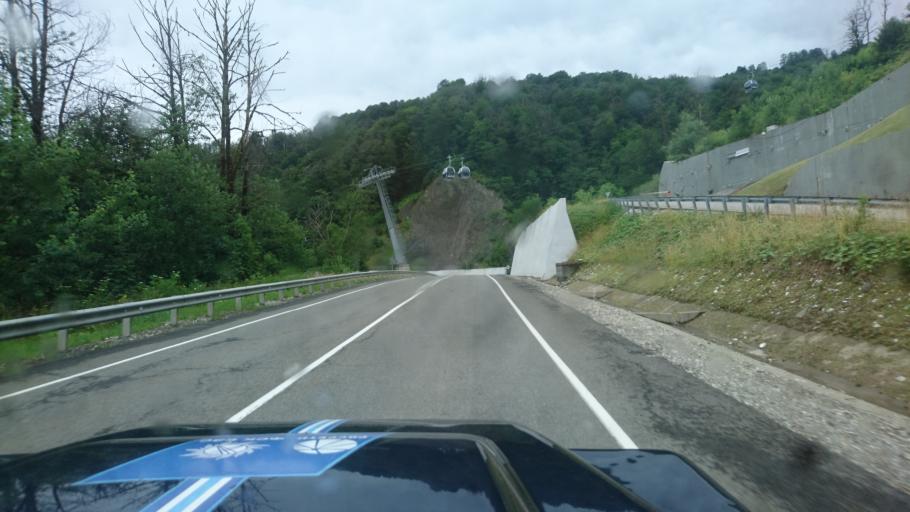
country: RU
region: Krasnodarskiy
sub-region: Sochi City
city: Krasnaya Polyana
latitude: 43.6676
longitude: 40.2917
